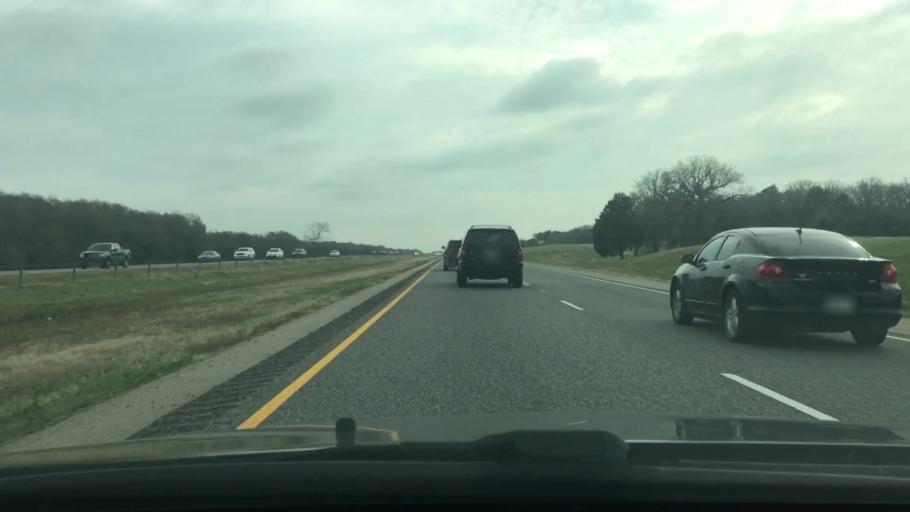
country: US
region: Texas
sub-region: Freestone County
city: Fairfield
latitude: 31.6232
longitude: -96.1575
